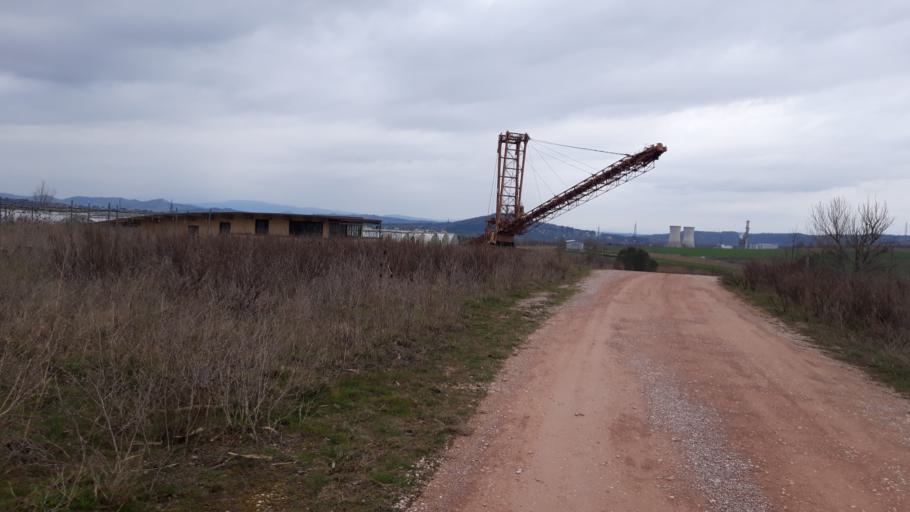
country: IT
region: Umbria
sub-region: Provincia di Perugia
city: Tavernelle
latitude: 42.9906
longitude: 12.1755
